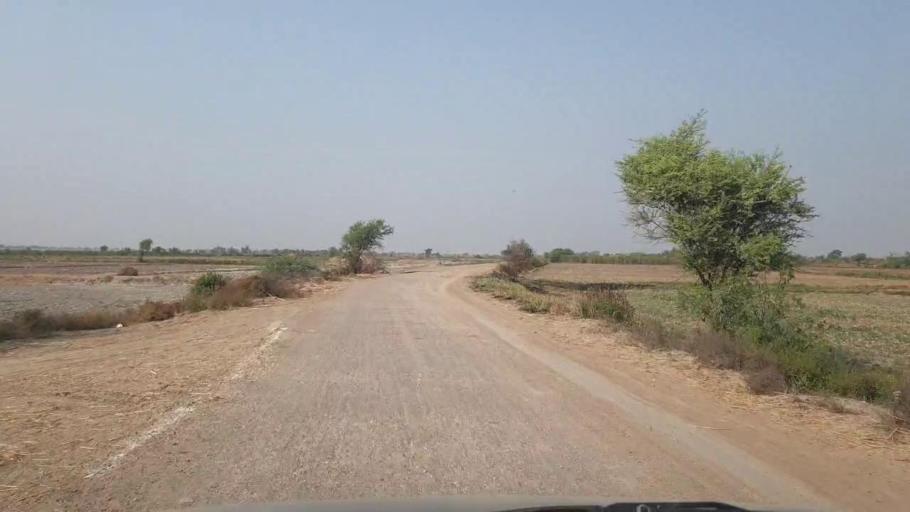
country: PK
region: Sindh
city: Tando Muhammad Khan
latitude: 25.0874
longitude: 68.3395
